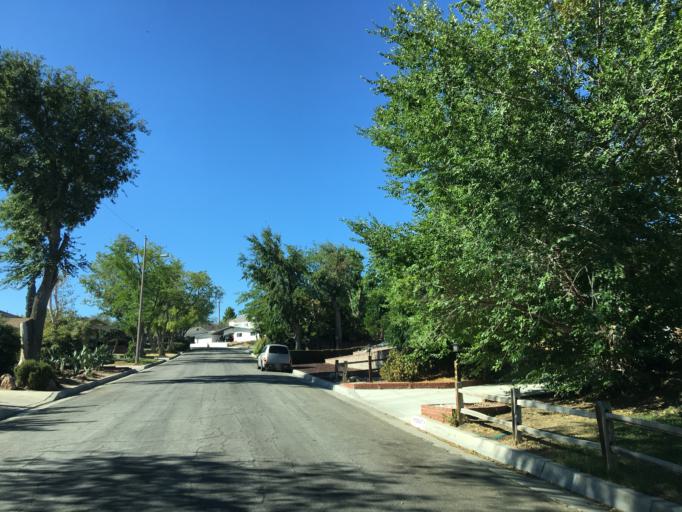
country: US
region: California
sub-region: Los Angeles County
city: Desert View Highlands
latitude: 34.5855
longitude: -118.1506
